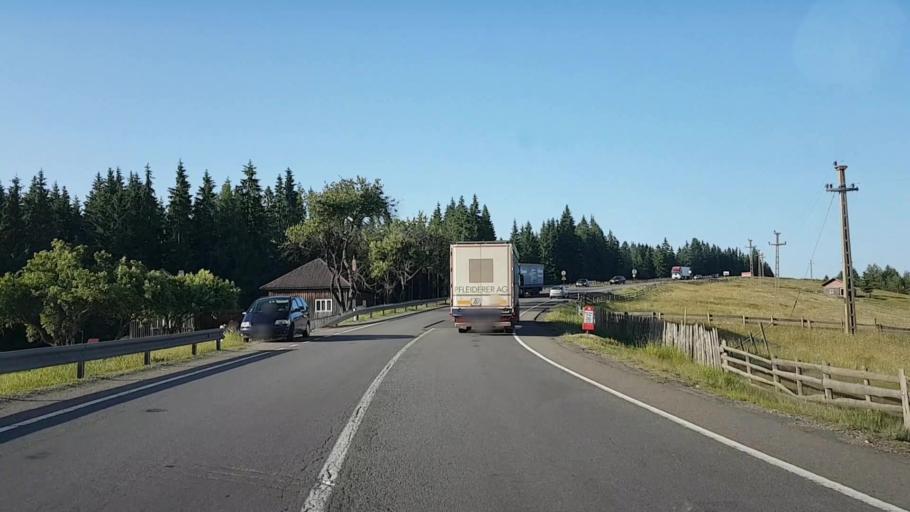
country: RO
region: Bistrita-Nasaud
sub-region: Comuna Lunca Ilvei
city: Lunca Ilvei
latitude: 47.2781
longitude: 25.0288
